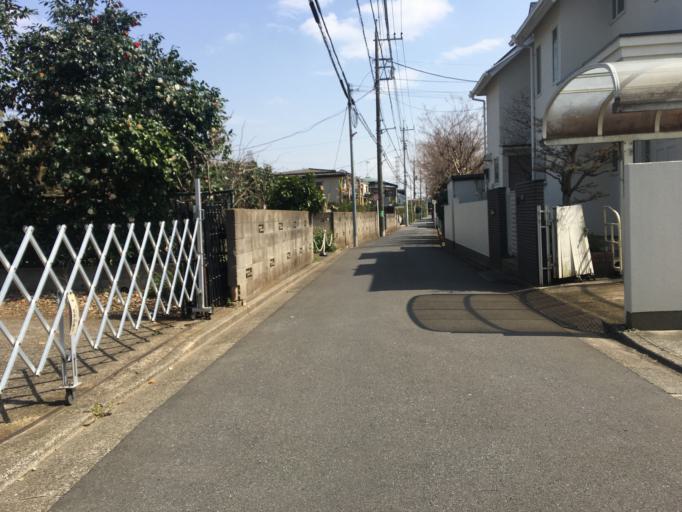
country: JP
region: Tokyo
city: Mitaka-shi
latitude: 35.6788
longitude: 139.5398
